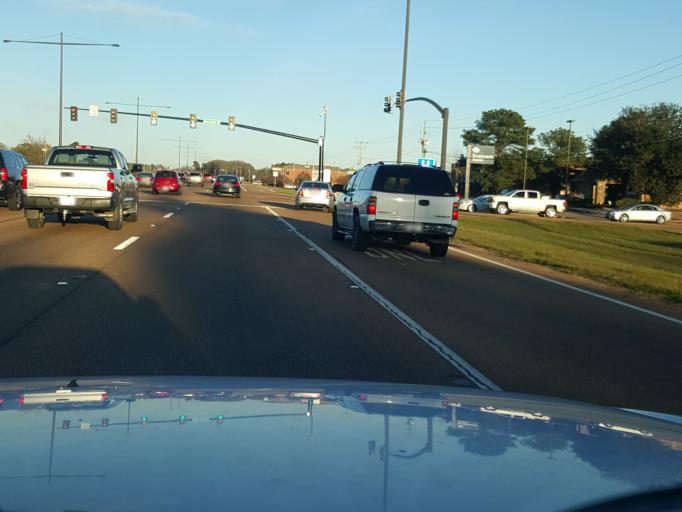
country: US
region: Mississippi
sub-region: Rankin County
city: Flowood
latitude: 32.3310
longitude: -90.1091
